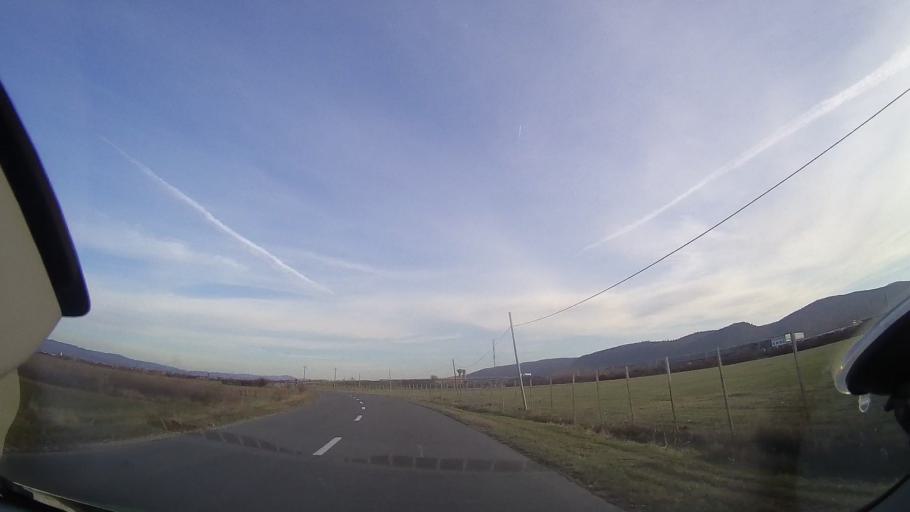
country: RO
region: Bihor
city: Lugasu de Jos
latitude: 47.0430
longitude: 22.3408
